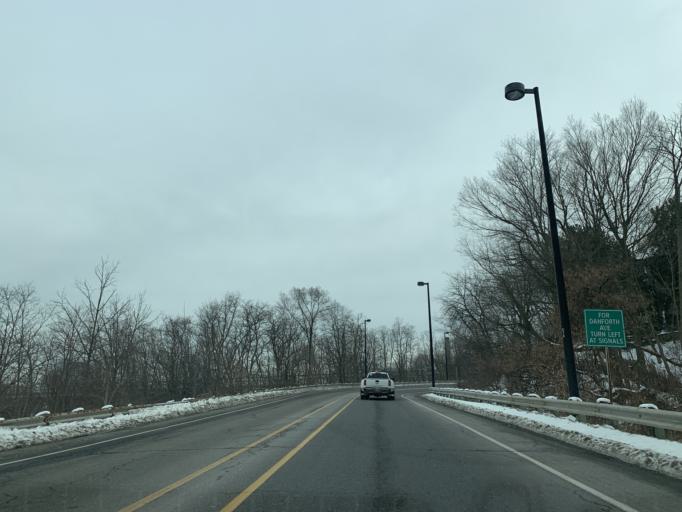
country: CA
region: Ontario
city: Toronto
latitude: 43.6765
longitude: -79.3675
